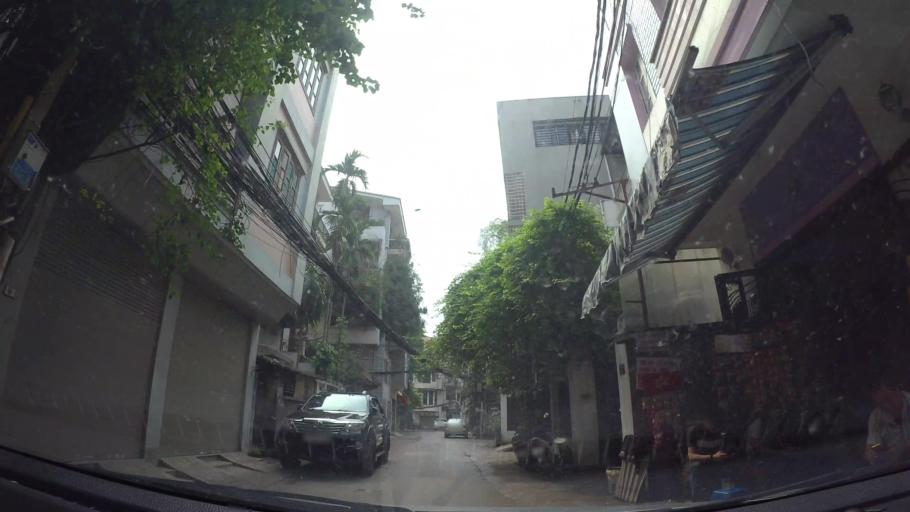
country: VN
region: Ha Noi
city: Hoan Kiem
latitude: 21.0501
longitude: 105.8435
